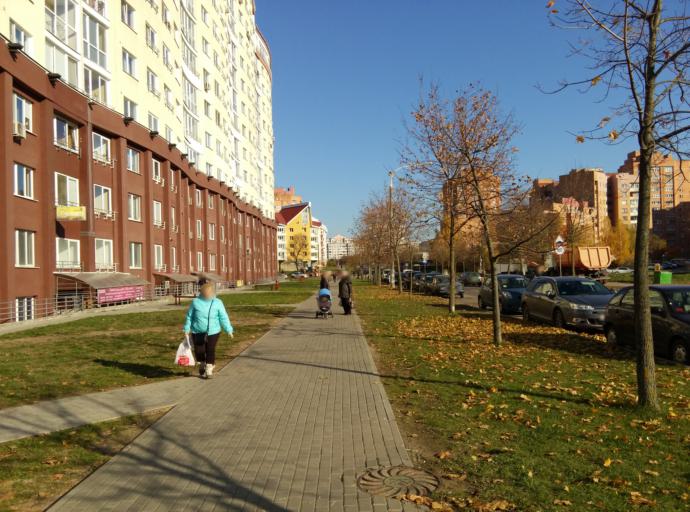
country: BY
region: Minsk
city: Borovlyany
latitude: 53.9481
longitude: 27.6816
